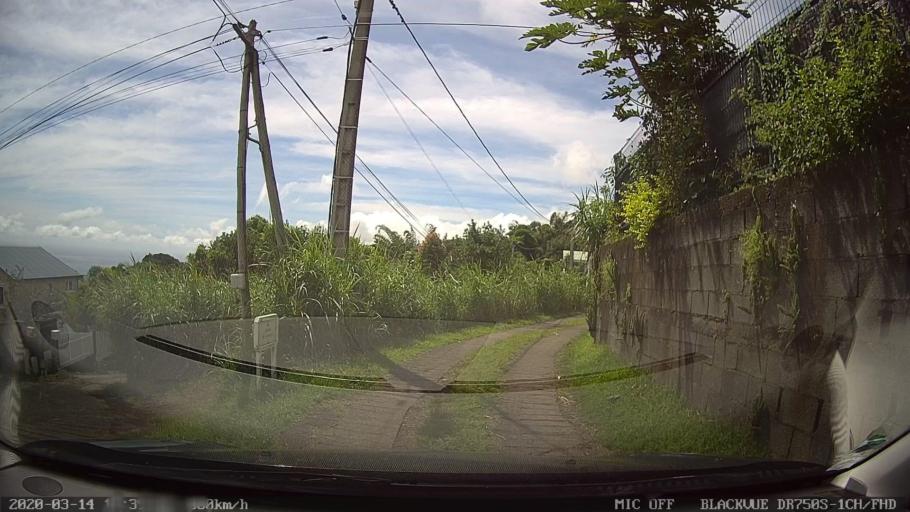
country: RE
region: Reunion
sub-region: Reunion
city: Sainte-Marie
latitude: -20.9461
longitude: 55.5245
